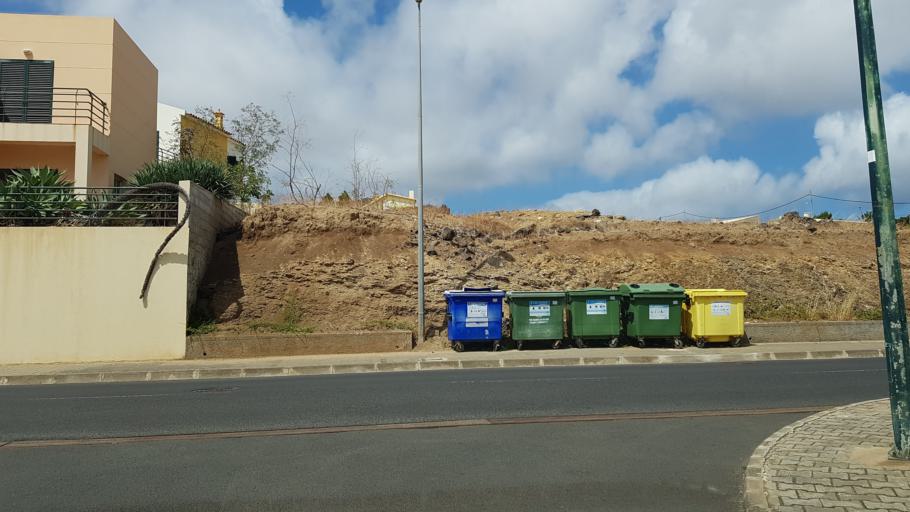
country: PT
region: Madeira
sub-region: Porto Santo
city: Vila de Porto Santo
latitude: 33.0610
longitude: -16.3417
